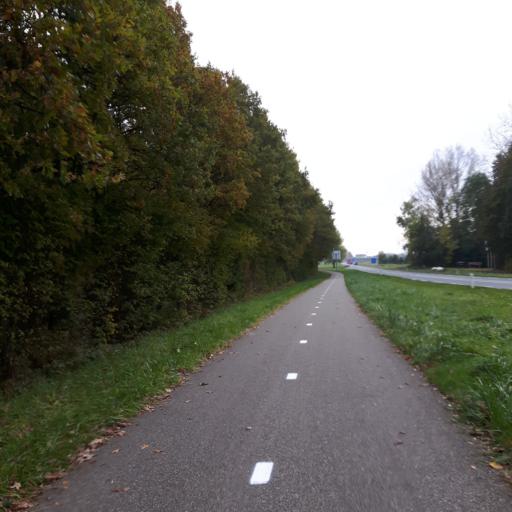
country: NL
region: Zeeland
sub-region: Gemeente Goes
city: Goes
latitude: 51.4897
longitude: 3.8116
